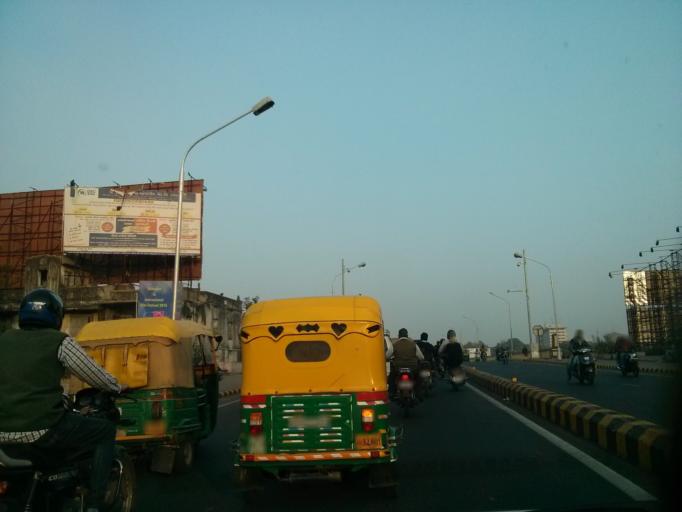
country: IN
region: Gujarat
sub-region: Ahmadabad
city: Ahmedabad
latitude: 23.0269
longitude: 72.5720
